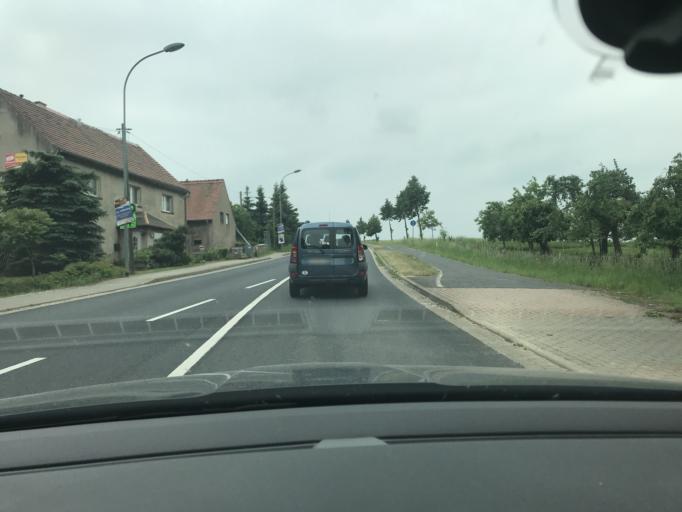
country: DE
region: Saxony
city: Priestewitz
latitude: 51.2278
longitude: 13.5053
